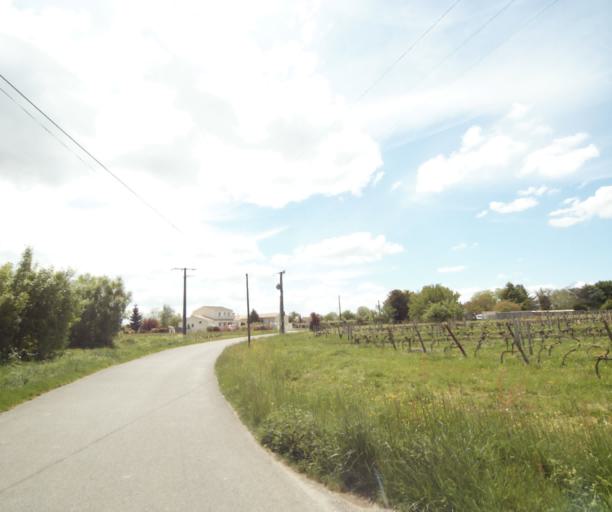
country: FR
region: Poitou-Charentes
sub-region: Departement de la Charente-Maritime
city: Burie
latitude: 45.7497
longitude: -0.4462
